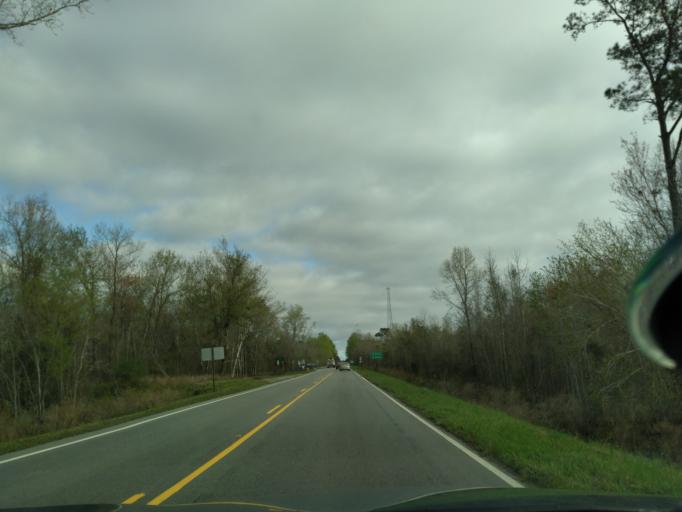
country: US
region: North Carolina
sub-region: Washington County
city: Plymouth
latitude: 35.9360
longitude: -76.7427
